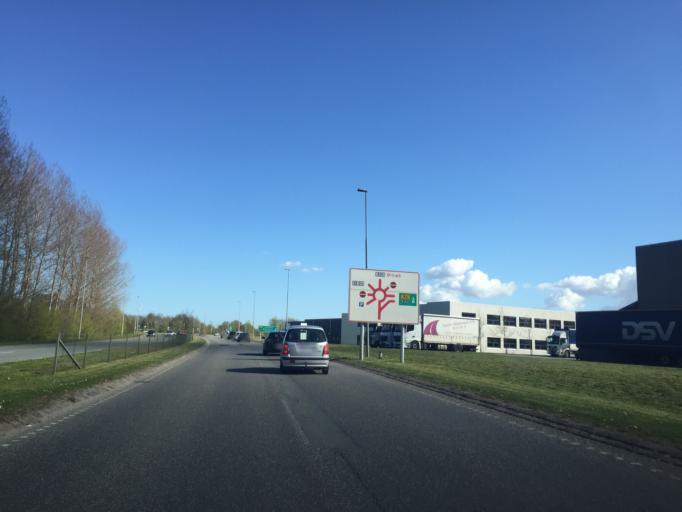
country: DK
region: South Denmark
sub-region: Odense Kommune
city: Neder Holluf
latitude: 55.3635
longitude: 10.4600
